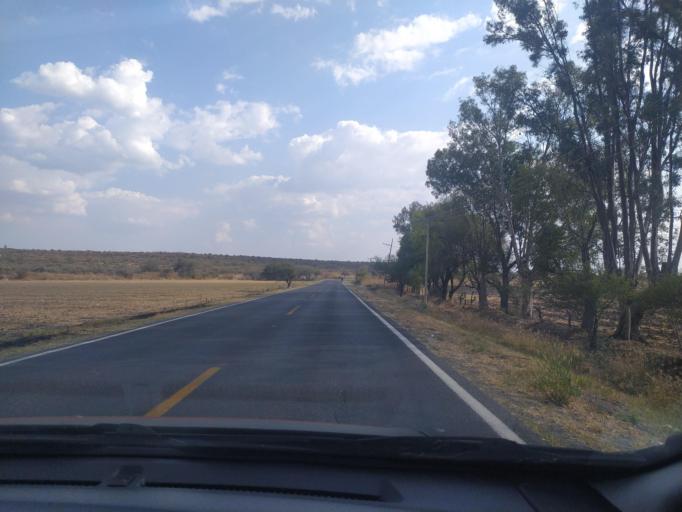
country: MX
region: Guanajuato
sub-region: San Francisco del Rincon
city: San Ignacio de Hidalgo
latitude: 20.9311
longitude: -101.8524
